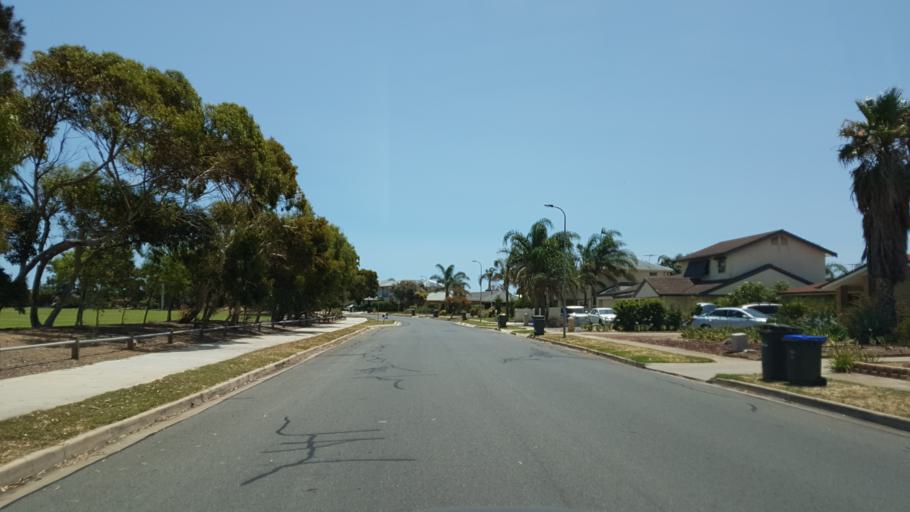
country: AU
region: South Australia
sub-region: Charles Sturt
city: West Lakes Shore
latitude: -34.8623
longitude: 138.4857
